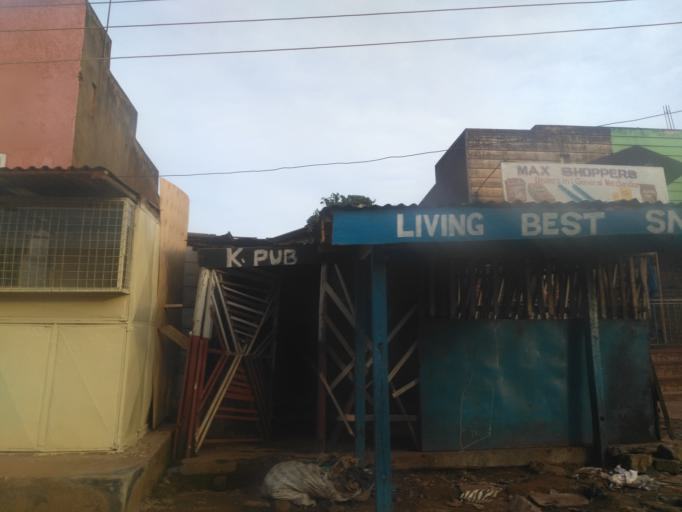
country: UG
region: Central Region
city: Kampala Central Division
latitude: 0.3433
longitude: 32.5762
